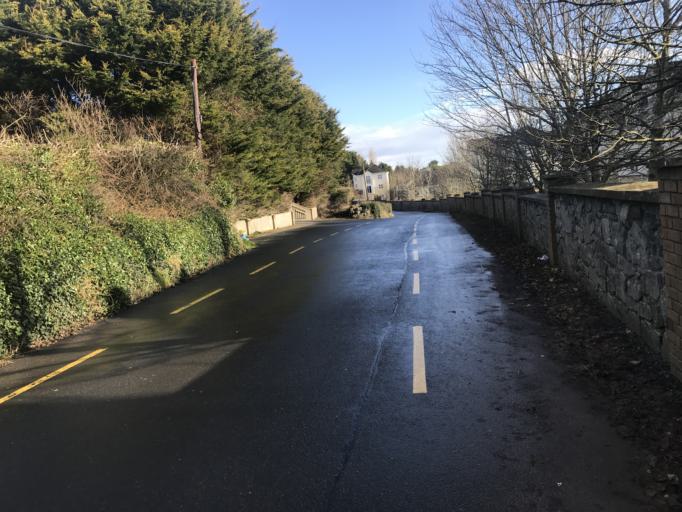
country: IE
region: Connaught
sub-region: County Galway
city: Gaillimh
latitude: 53.2981
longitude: -9.0287
